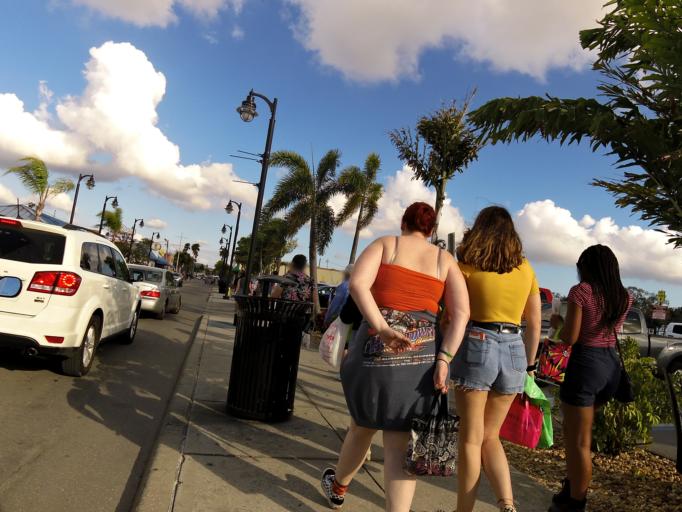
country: US
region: Florida
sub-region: Pinellas County
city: Tarpon Springs
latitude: 28.1555
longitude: -82.7597
